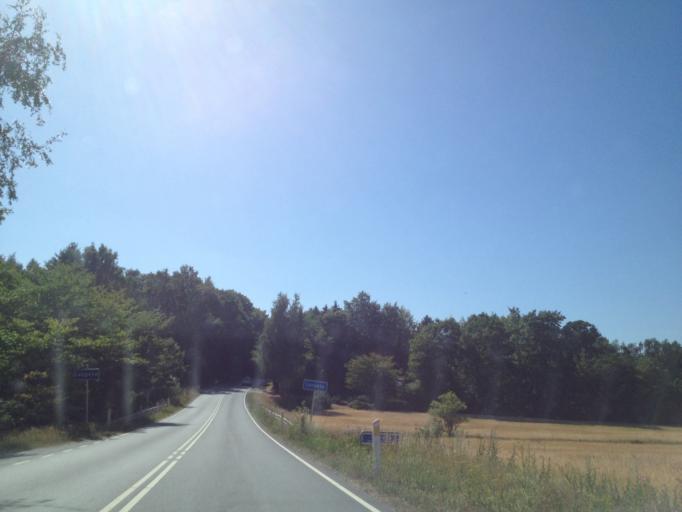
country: DK
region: Capital Region
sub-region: Helsingor Kommune
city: Hornbaek
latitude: 56.0399
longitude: 12.4513
